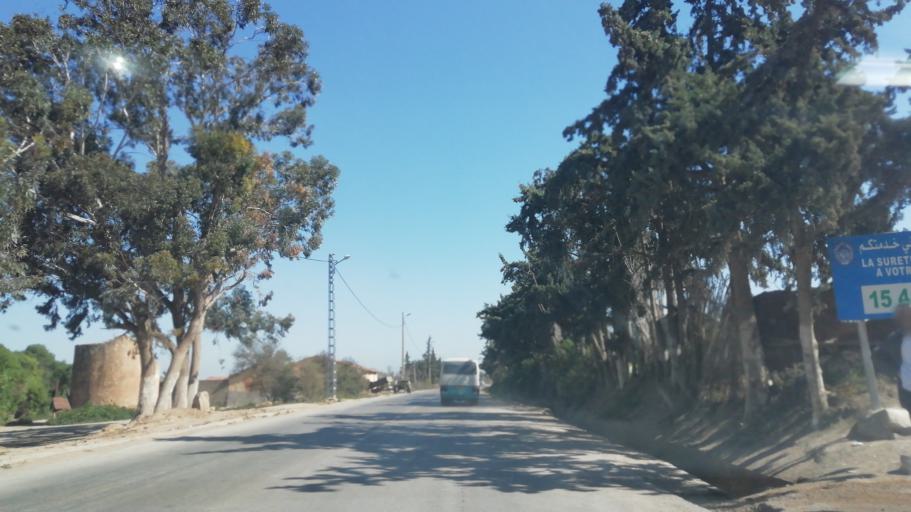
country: DZ
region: Mascara
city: Sig
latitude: 35.5645
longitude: -0.0876
